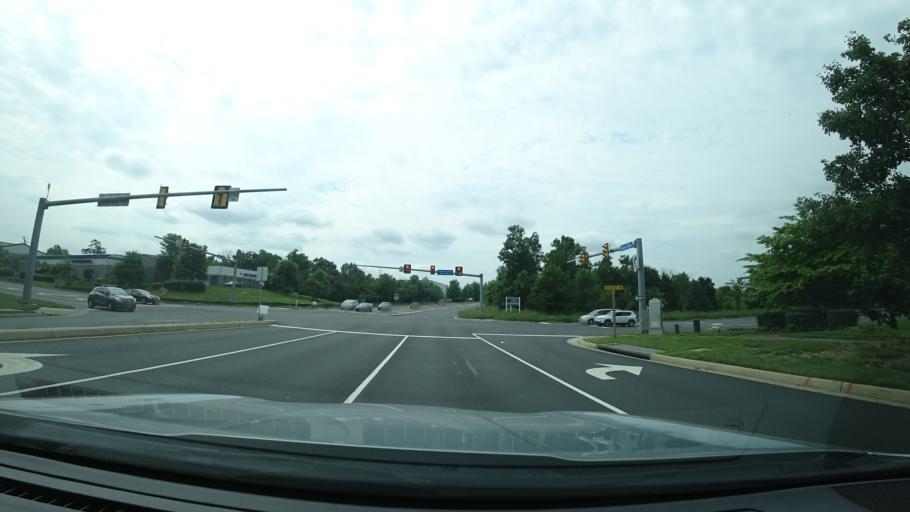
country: US
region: Virginia
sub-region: Loudoun County
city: Sterling
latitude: 39.0213
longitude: -77.4244
